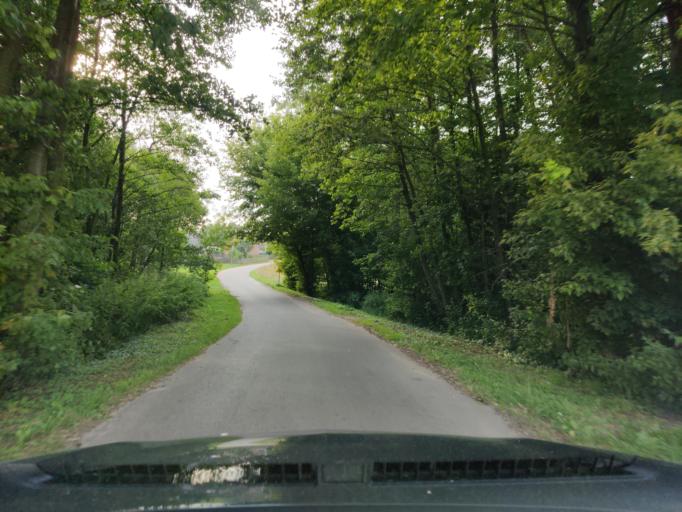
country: PL
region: Masovian Voivodeship
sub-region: Powiat pultuski
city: Obryte
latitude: 52.7418
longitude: 21.2499
